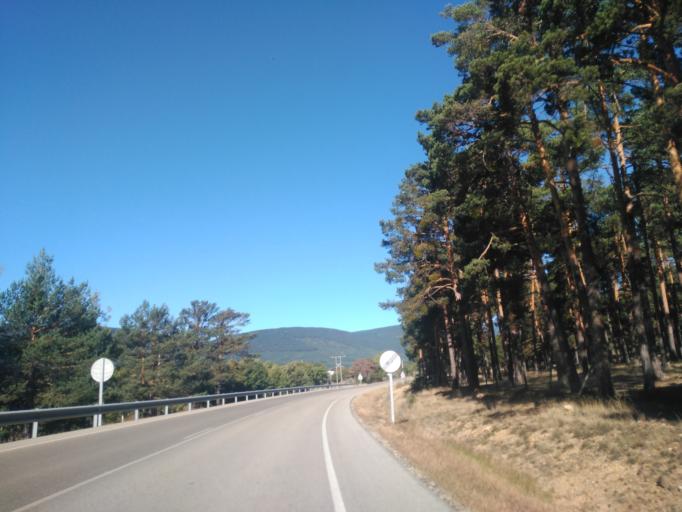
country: ES
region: Castille and Leon
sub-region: Provincia de Soria
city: Vinuesa
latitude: 41.9011
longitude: -2.7390
